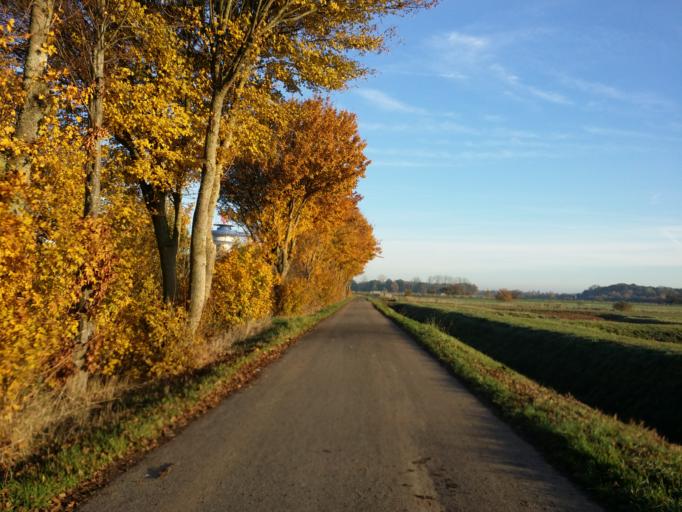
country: DE
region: Bremen
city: Bremen
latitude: 53.0315
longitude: 8.7988
